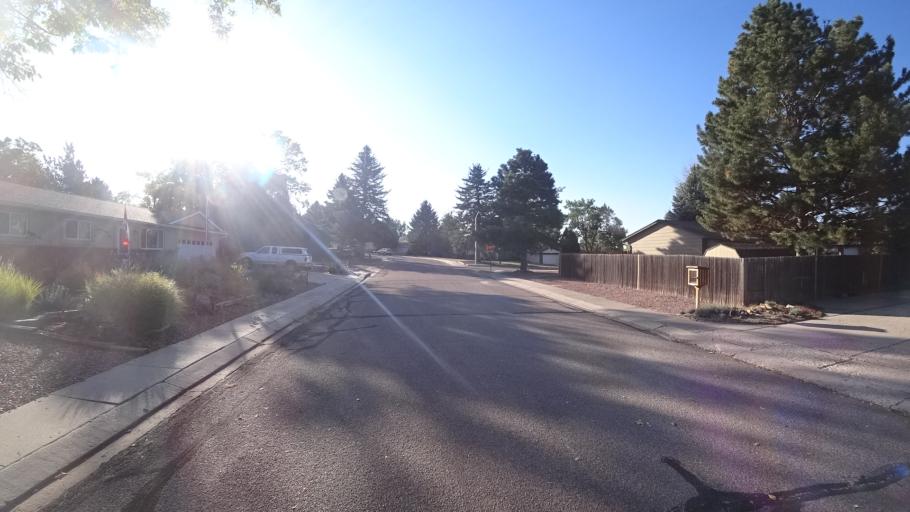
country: US
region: Colorado
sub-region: El Paso County
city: Cimarron Hills
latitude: 38.8822
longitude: -104.7467
